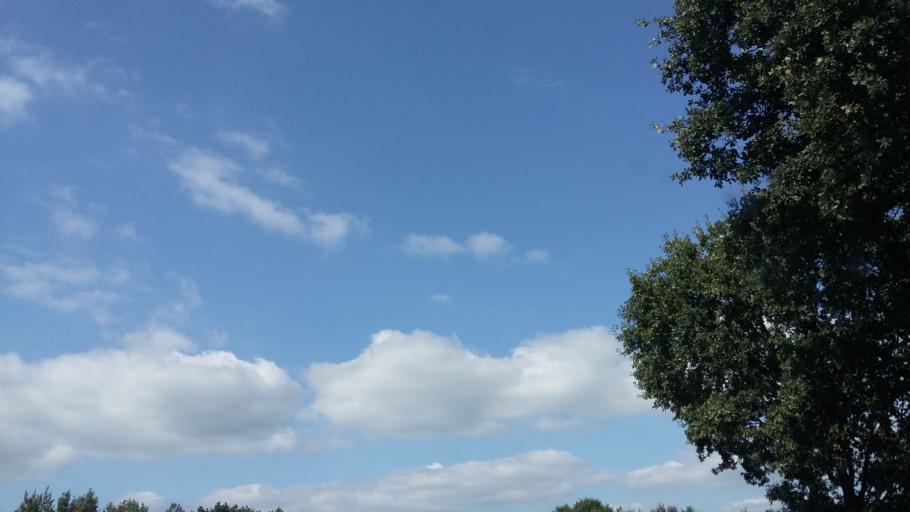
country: DE
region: Bremen
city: Bremen
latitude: 53.1161
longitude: 8.8120
